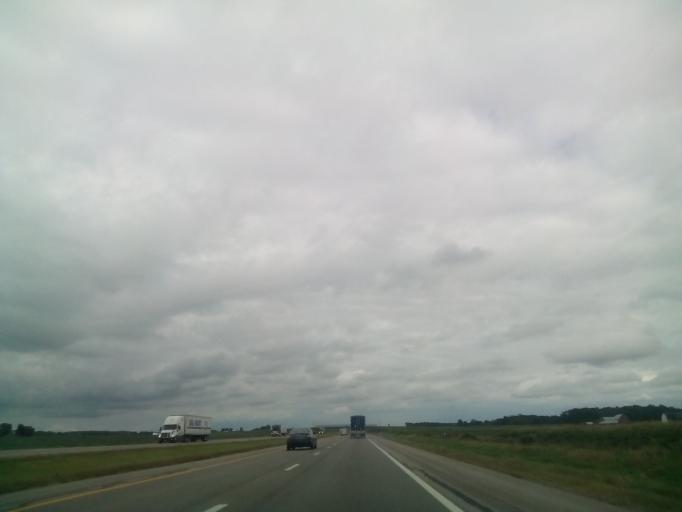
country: US
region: Ohio
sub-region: Fulton County
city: Burlington
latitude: 41.5904
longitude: -84.2766
